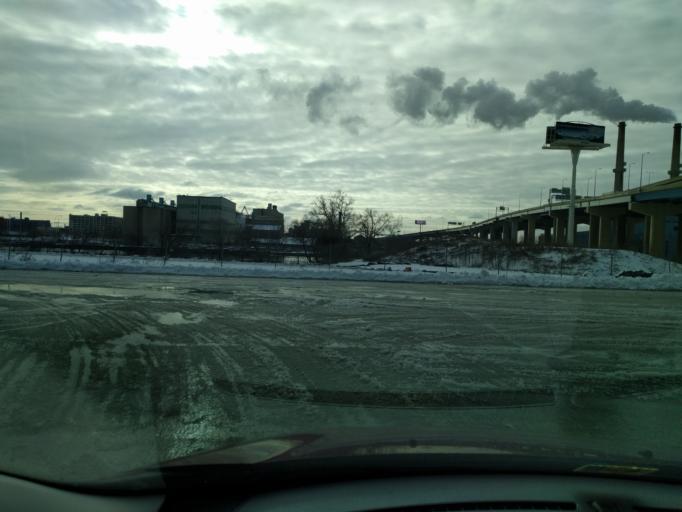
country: US
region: Wisconsin
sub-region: Milwaukee County
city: Milwaukee
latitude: 43.0344
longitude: -87.9207
